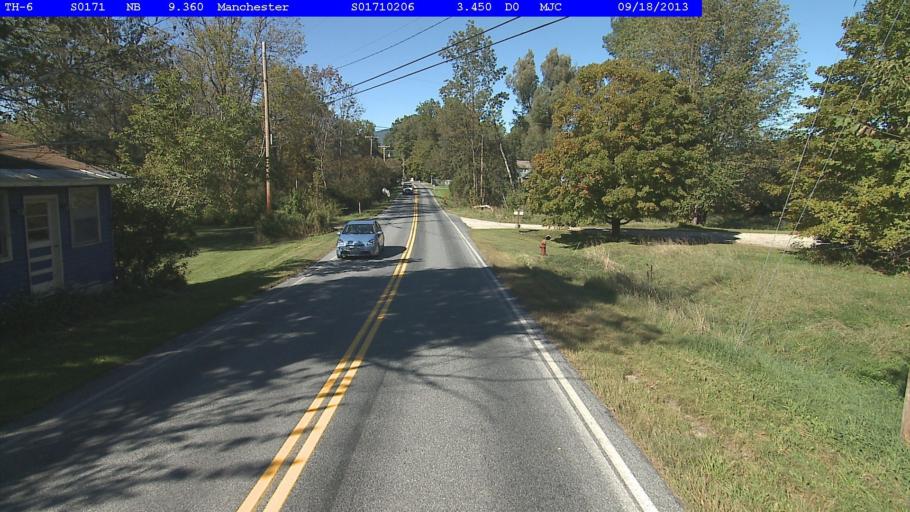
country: US
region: Vermont
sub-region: Bennington County
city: Manchester Center
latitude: 43.1542
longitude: -73.0516
